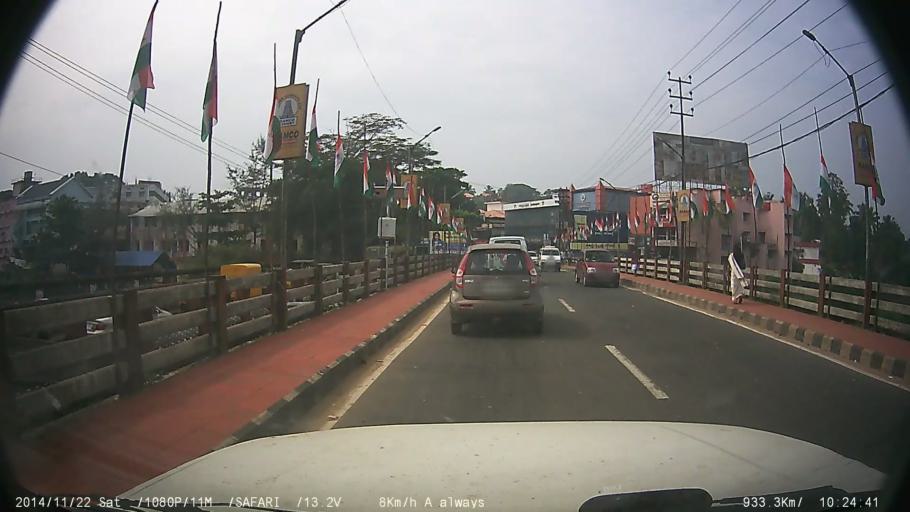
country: IN
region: Kerala
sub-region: Ernakulam
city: Muvattupula
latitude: 9.9882
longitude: 76.5782
